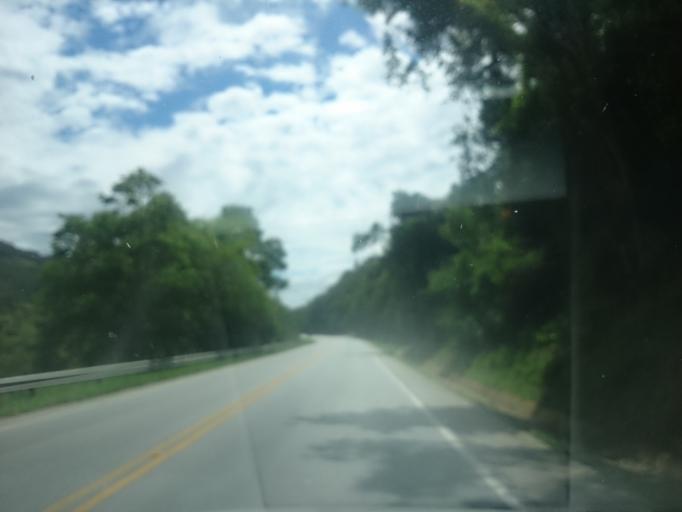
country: BR
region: Santa Catarina
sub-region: Anitapolis
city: Anitapolis
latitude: -27.7131
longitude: -49.2623
